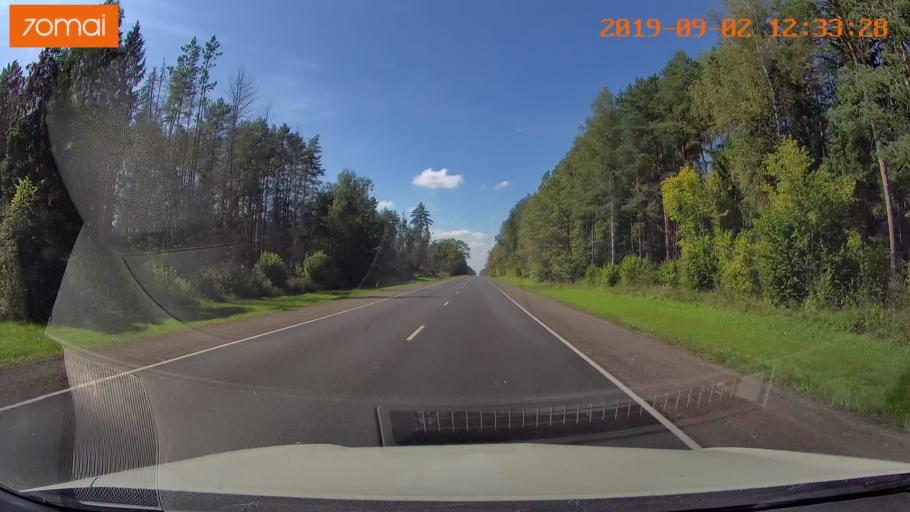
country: RU
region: Smolensk
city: Shumyachi
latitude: 53.8177
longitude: 32.4280
